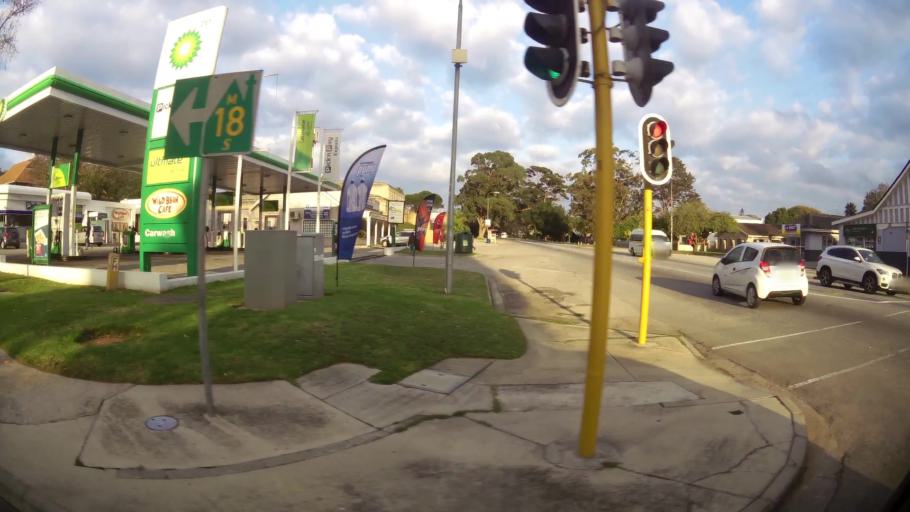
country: ZA
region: Eastern Cape
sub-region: Nelson Mandela Bay Metropolitan Municipality
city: Port Elizabeth
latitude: -33.9805
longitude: 25.5800
